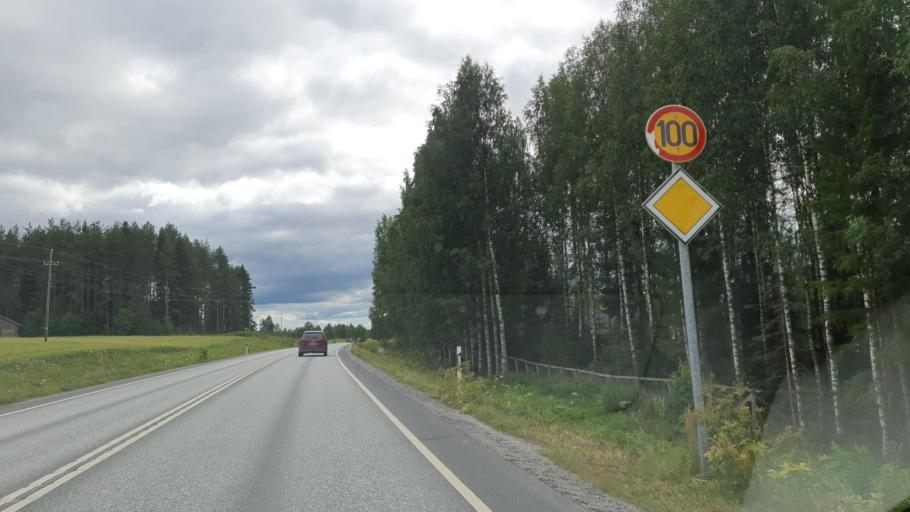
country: FI
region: Northern Savo
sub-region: Ylae-Savo
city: Sonkajaervi
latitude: 63.8483
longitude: 27.4392
